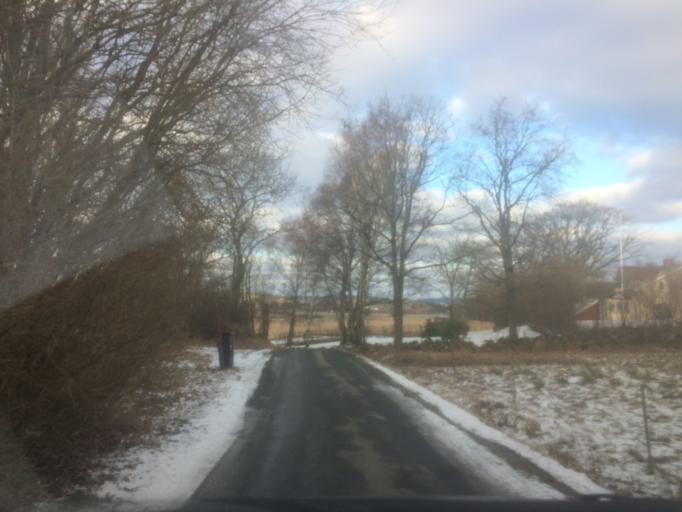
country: SE
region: Vaestra Goetaland
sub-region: Kungalvs Kommun
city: Kungalv
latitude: 57.8414
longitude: 11.9436
